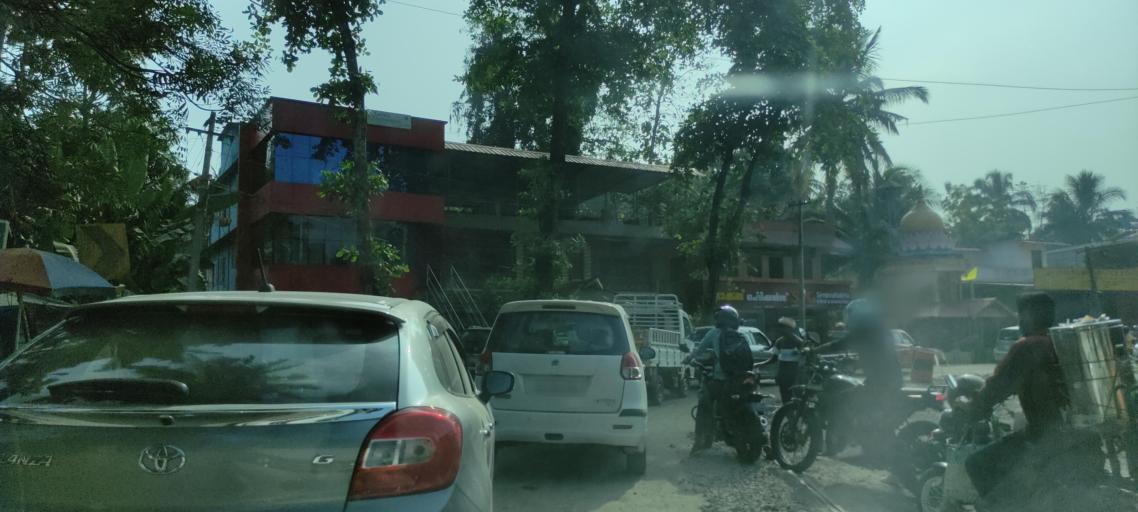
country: IN
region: Kerala
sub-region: Pattanamtitta
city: Tiruvalla
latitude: 9.3663
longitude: 76.5465
